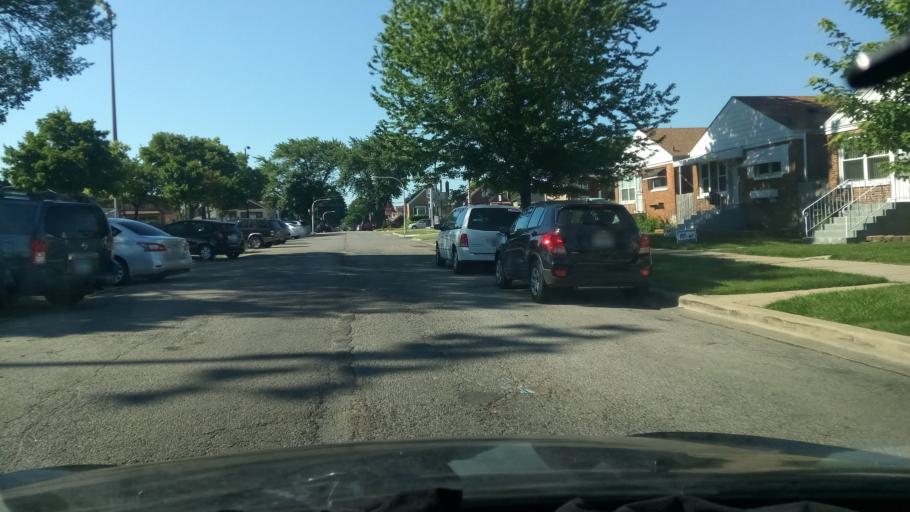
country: US
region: Illinois
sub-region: Cook County
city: Hometown
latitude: 41.7722
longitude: -87.7299
